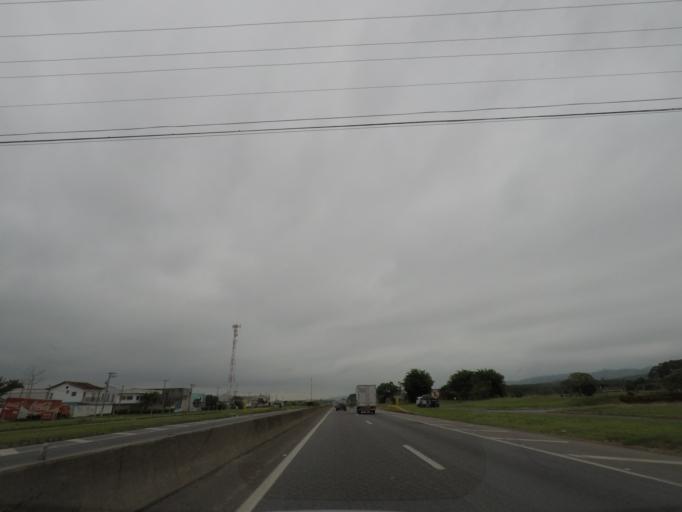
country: BR
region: Sao Paulo
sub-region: Pindamonhangaba
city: Pindamonhangaba
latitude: -22.9524
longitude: -45.4049
